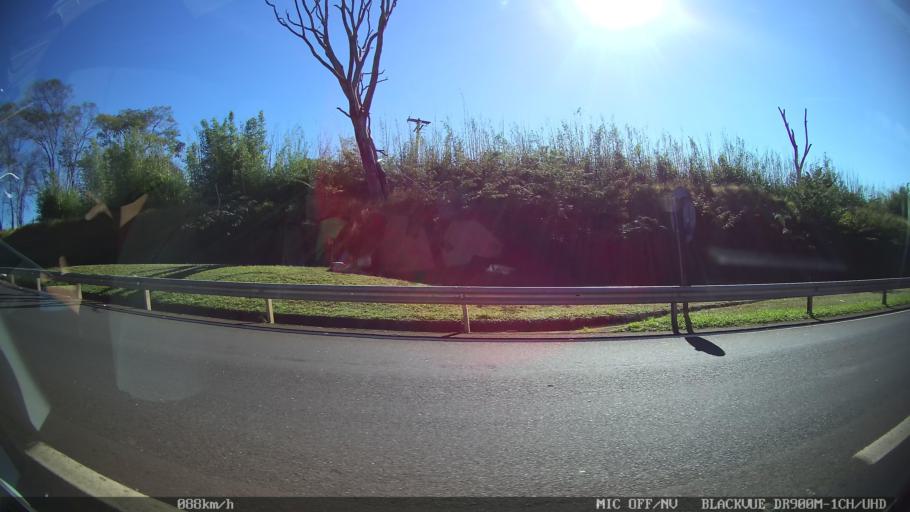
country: BR
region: Sao Paulo
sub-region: Franca
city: Franca
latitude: -20.5747
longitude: -47.3648
